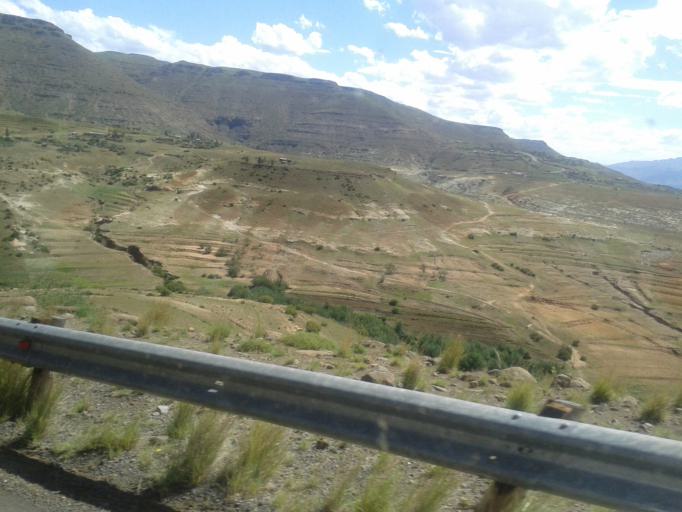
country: LS
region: Qacha's Nek
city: Qacha's Nek
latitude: -30.0498
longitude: 28.3040
